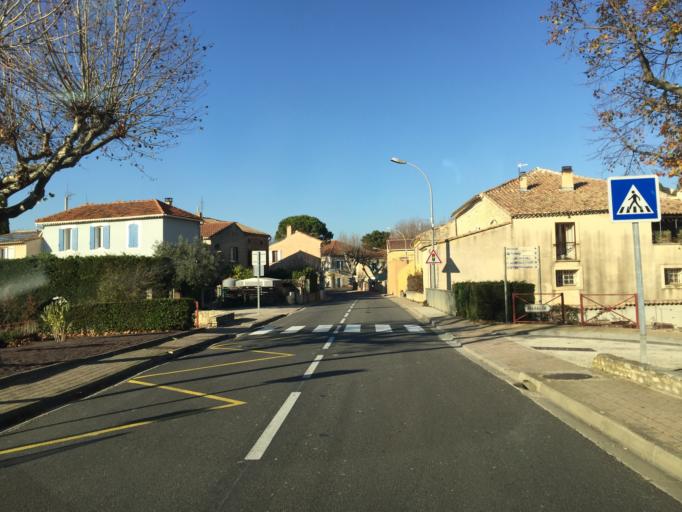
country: FR
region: Provence-Alpes-Cote d'Azur
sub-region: Departement du Vaucluse
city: Sainte-Cecile-les-Vignes
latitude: 44.2289
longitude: 4.9324
